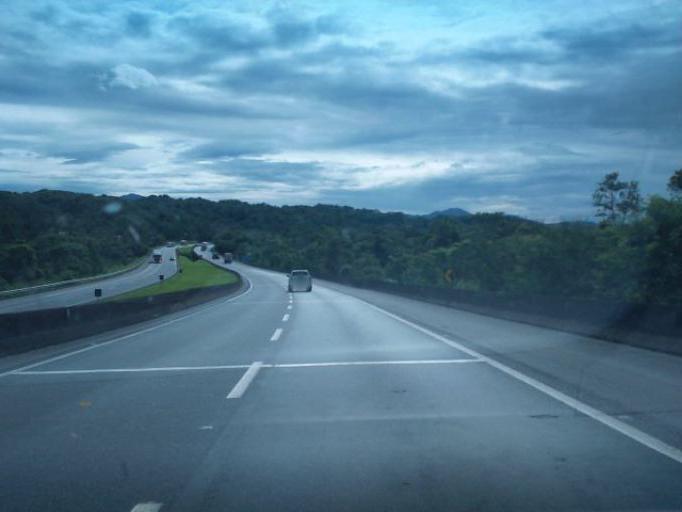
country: BR
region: Sao Paulo
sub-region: Cajati
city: Cajati
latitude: -24.9696
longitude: -48.3659
